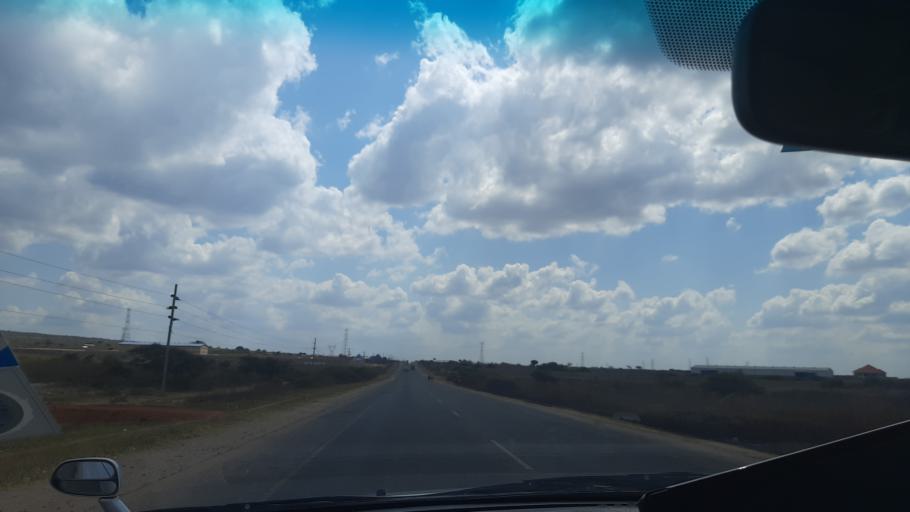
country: TZ
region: Dodoma
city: Dodoma
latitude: -6.1286
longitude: 35.6770
